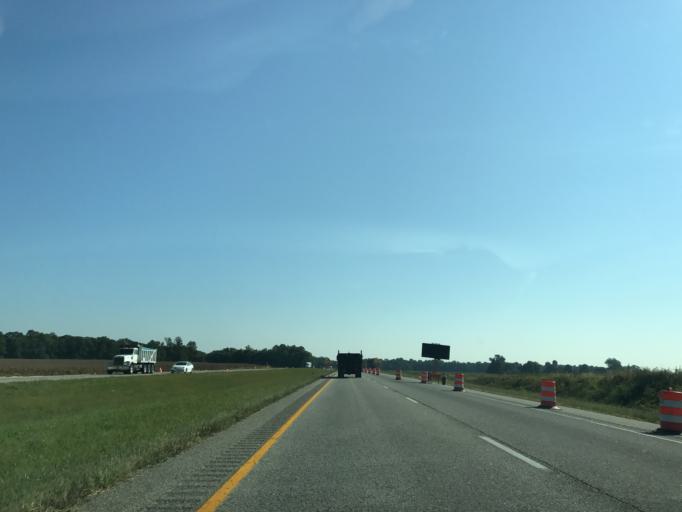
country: US
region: Maryland
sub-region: Queen Anne's County
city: Centreville
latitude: 39.0170
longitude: -76.0554
